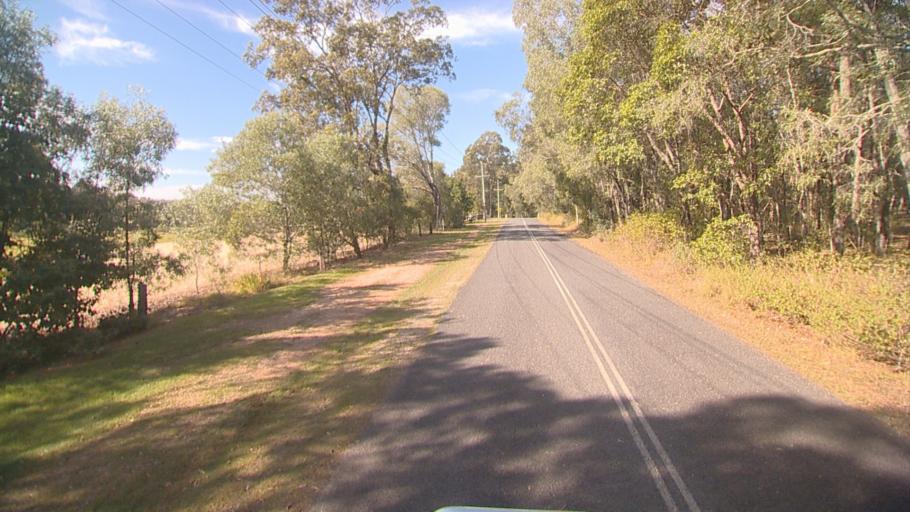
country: AU
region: Queensland
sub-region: Logan
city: Windaroo
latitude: -27.7777
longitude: 153.1803
